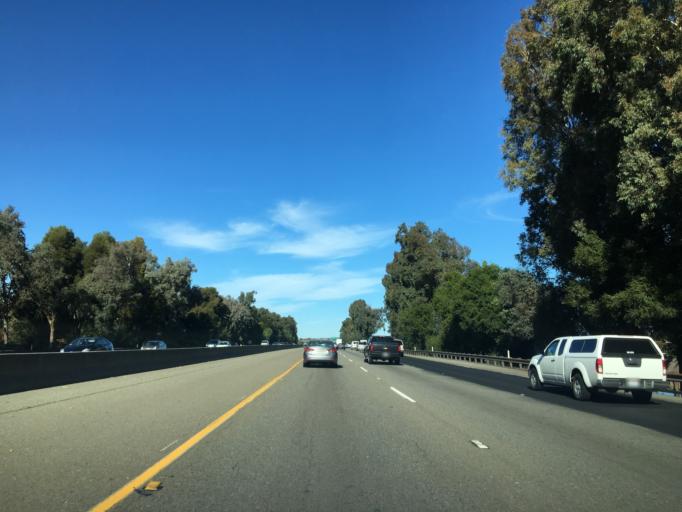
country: US
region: California
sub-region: Alameda County
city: Dublin
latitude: 37.6811
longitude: -121.9148
